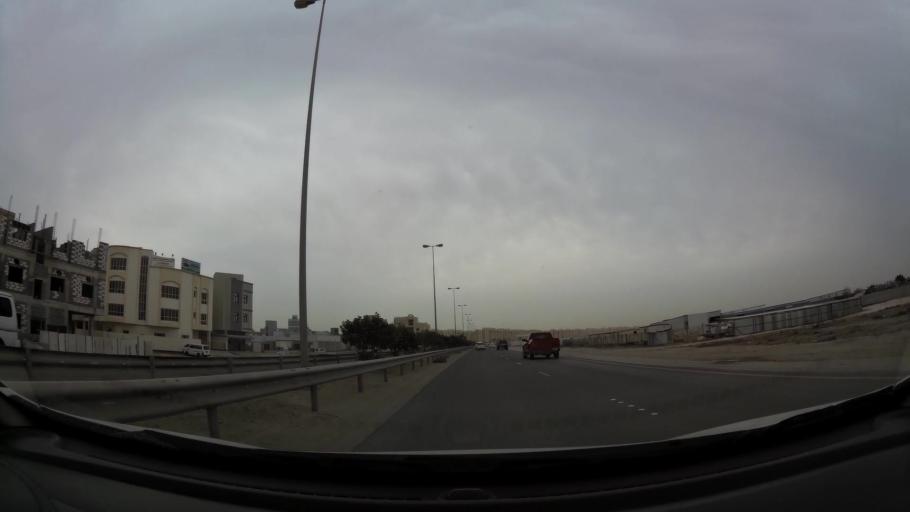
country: BH
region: Northern
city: Madinat `Isa
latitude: 26.1812
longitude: 50.5204
